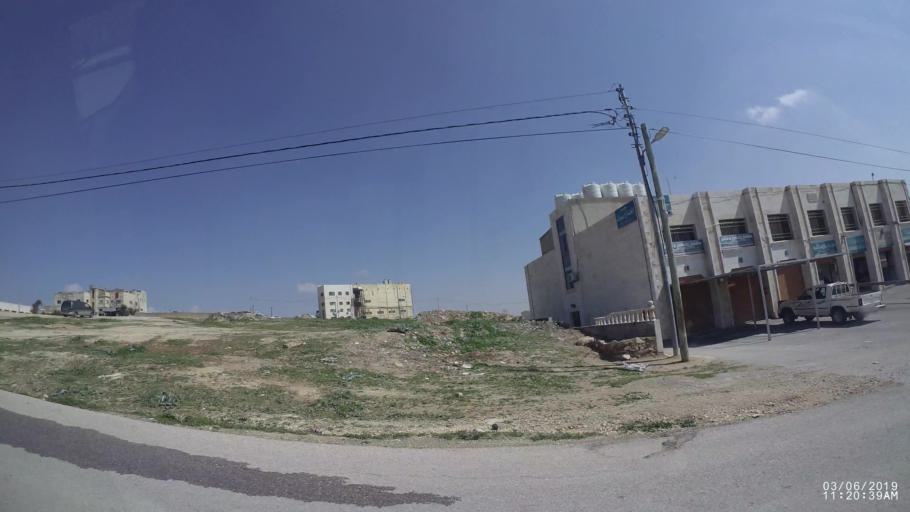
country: JO
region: Amman
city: Amman
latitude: 31.9786
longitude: 35.9990
